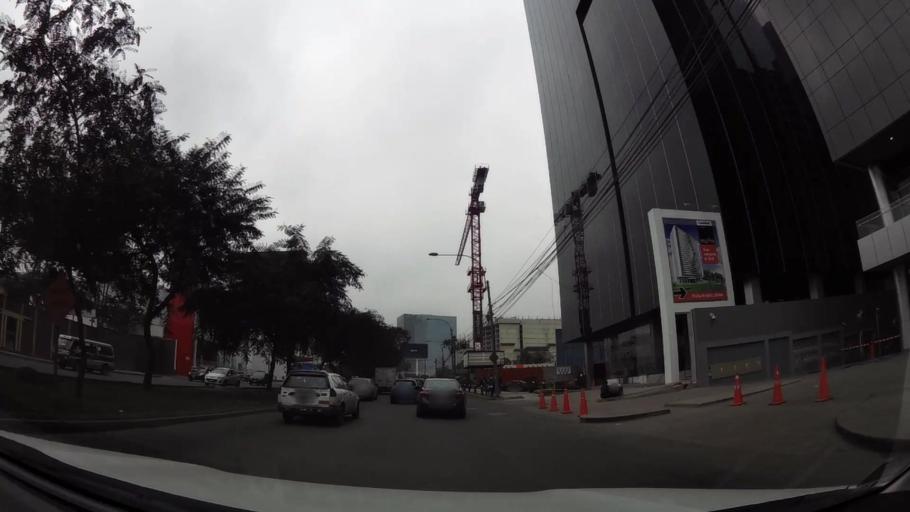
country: PE
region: Lima
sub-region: Lima
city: La Molina
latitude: -12.0825
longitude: -76.9687
